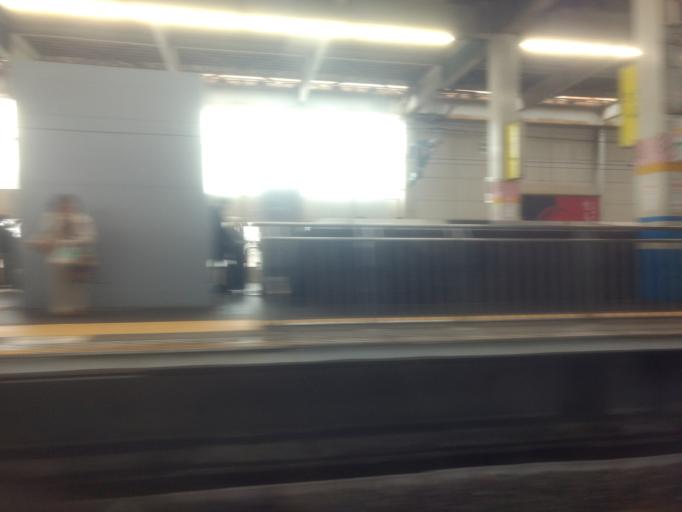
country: JP
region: Hiroshima
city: Hiroshima-shi
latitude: 34.3983
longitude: 132.4758
